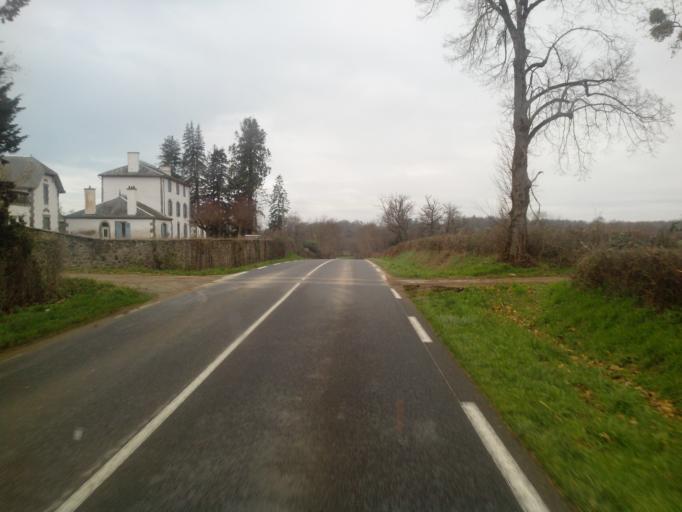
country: FR
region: Limousin
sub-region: Departement de la Haute-Vienne
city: Magnac-Laval
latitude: 46.2136
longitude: 1.1460
